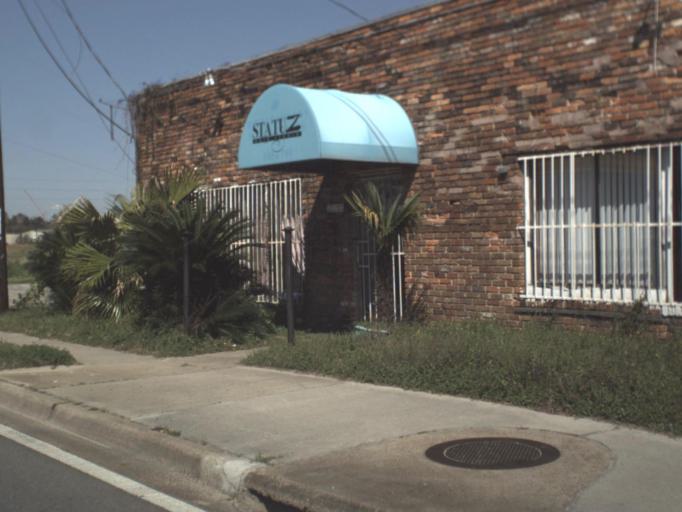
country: US
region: Florida
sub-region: Leon County
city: Tallahassee
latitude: 30.4287
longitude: -84.3022
